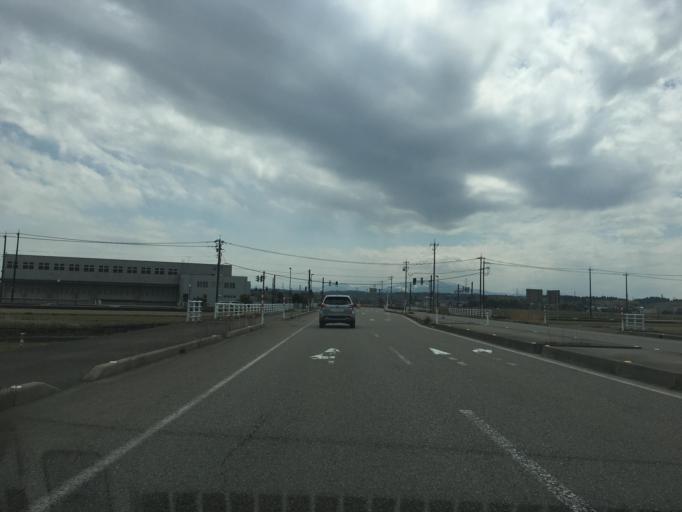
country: JP
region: Toyama
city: Kuragaki-kosugi
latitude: 36.7122
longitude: 137.1173
